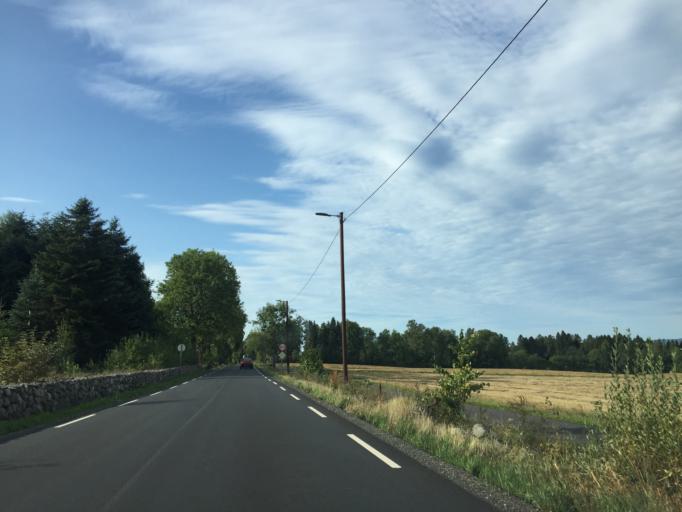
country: NO
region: Akershus
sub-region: As
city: As
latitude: 59.7137
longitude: 10.7735
